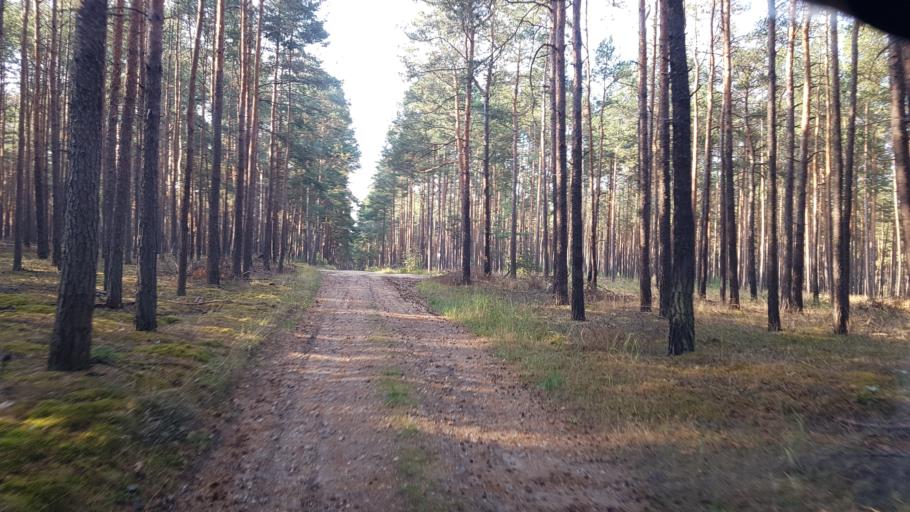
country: DE
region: Brandenburg
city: Sonnewalde
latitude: 51.6447
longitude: 13.6485
